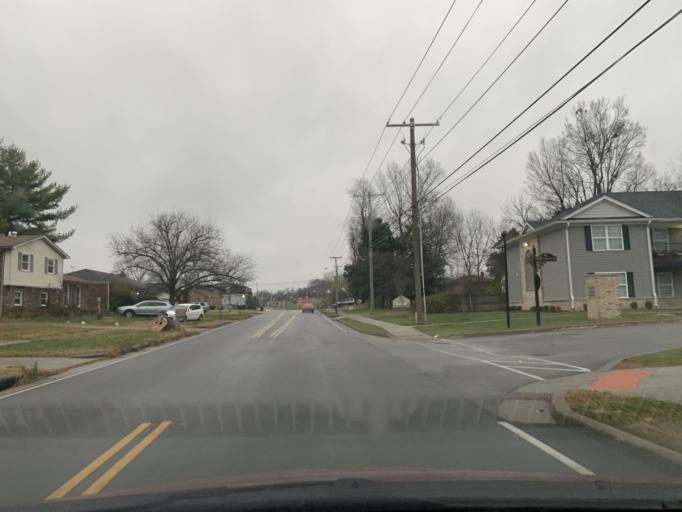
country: US
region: Kentucky
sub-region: Jefferson County
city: Buechel
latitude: 38.1976
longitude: -85.6277
